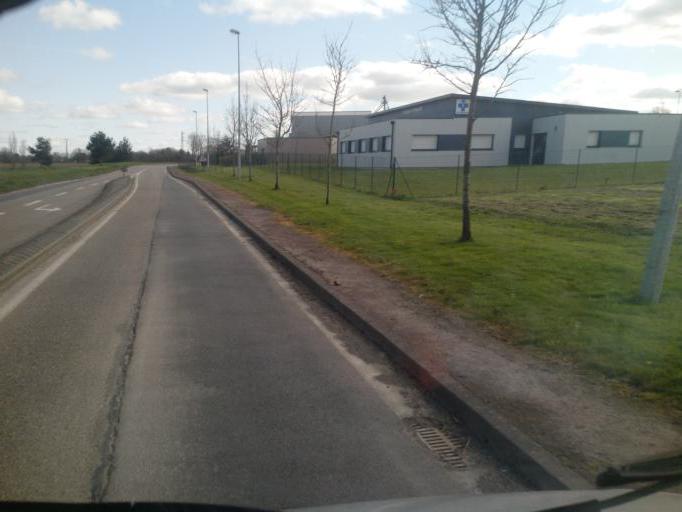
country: FR
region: Brittany
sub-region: Departement d'Ille-et-Vilaine
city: Plelan-le-Grand
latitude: 48.0018
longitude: -2.0844
